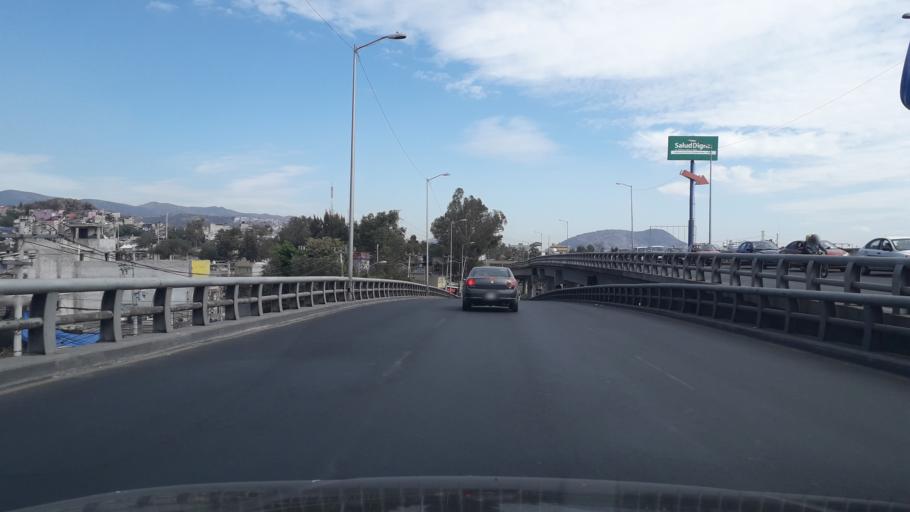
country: MX
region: Mexico City
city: Gustavo A. Madero
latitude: 19.5096
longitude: -99.0905
